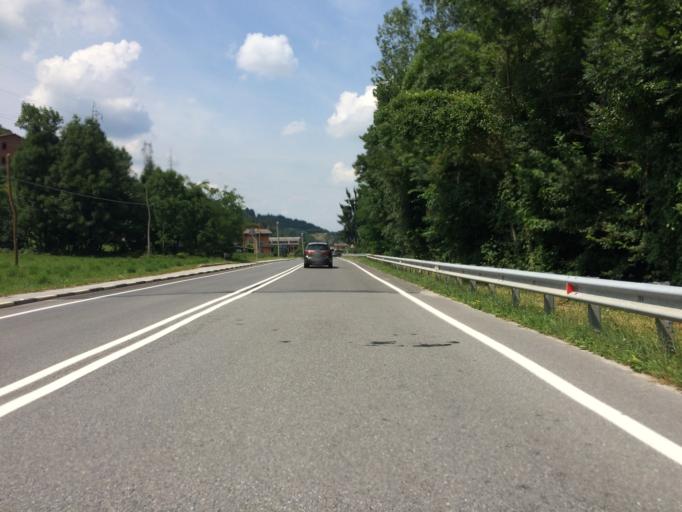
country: IT
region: Piedmont
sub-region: Provincia di Cuneo
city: Robilante
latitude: 44.2753
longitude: 7.5187
